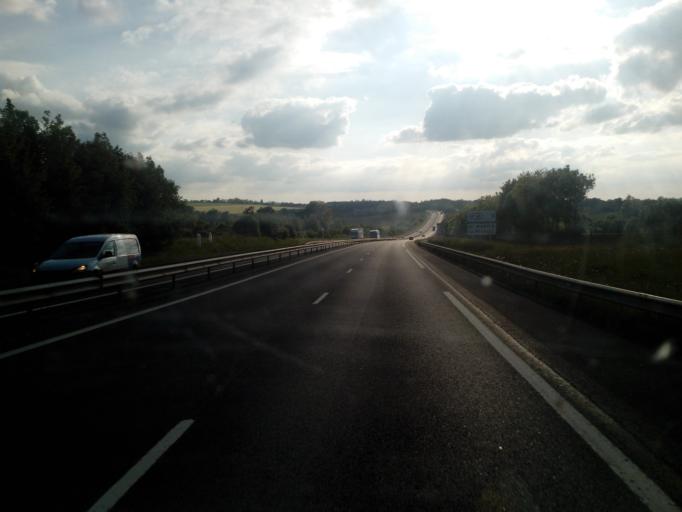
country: FR
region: Lower Normandy
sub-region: Departement du Calvados
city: Cahagnes
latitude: 49.0503
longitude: -0.7293
